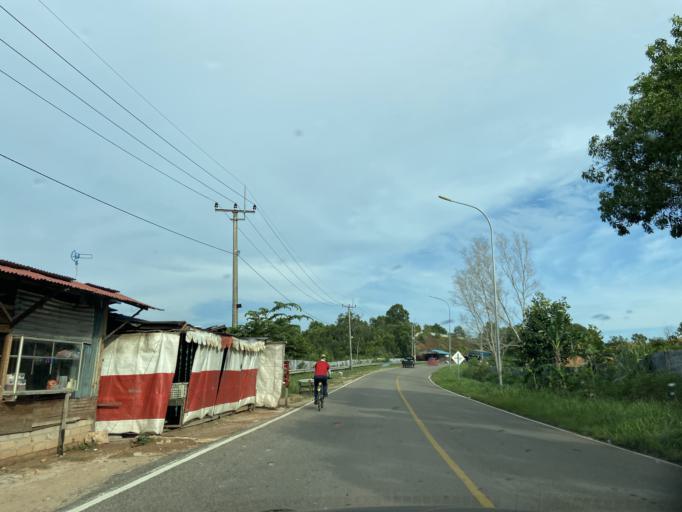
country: SG
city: Singapore
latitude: 0.9769
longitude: 104.0460
